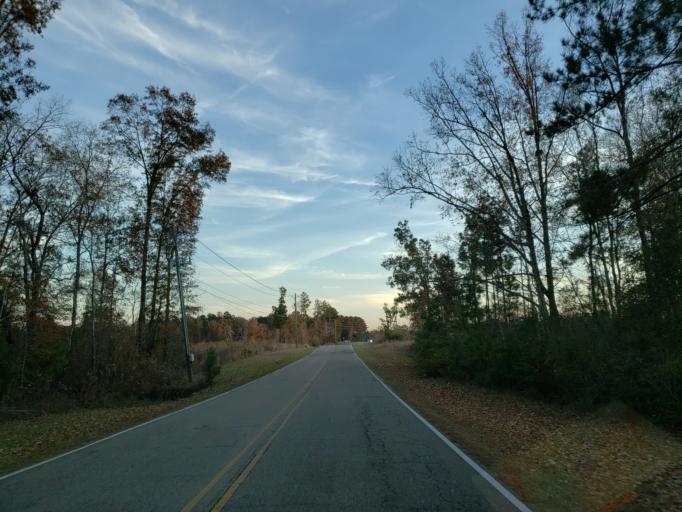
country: US
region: Mississippi
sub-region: Forrest County
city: Hattiesburg
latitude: 31.2935
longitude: -89.3146
